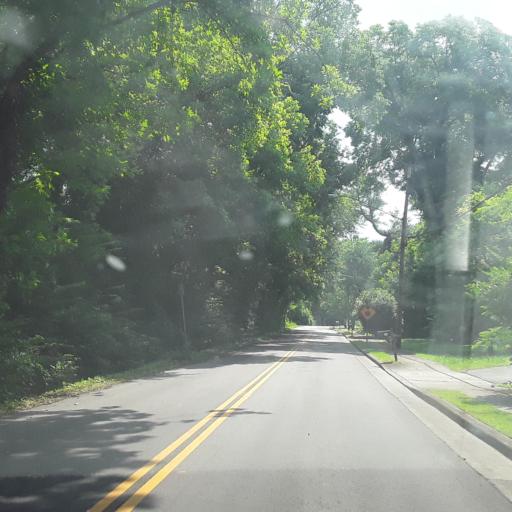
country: US
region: Tennessee
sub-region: Davidson County
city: Oak Hill
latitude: 36.1163
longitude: -86.7328
